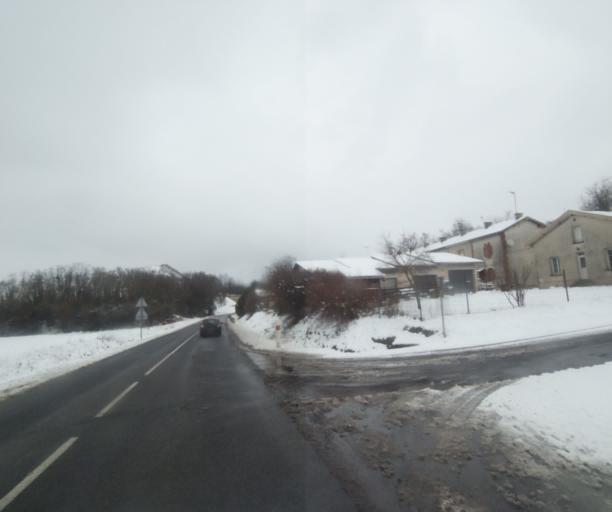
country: FR
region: Champagne-Ardenne
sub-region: Departement de la Haute-Marne
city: Wassy
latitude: 48.4839
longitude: 4.9692
